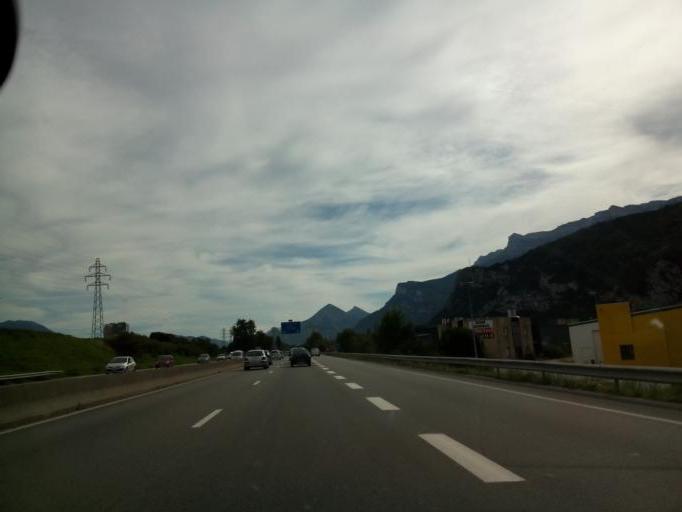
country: FR
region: Rhone-Alpes
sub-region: Departement de l'Isere
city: Seyssins
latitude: 45.1536
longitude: 5.6982
